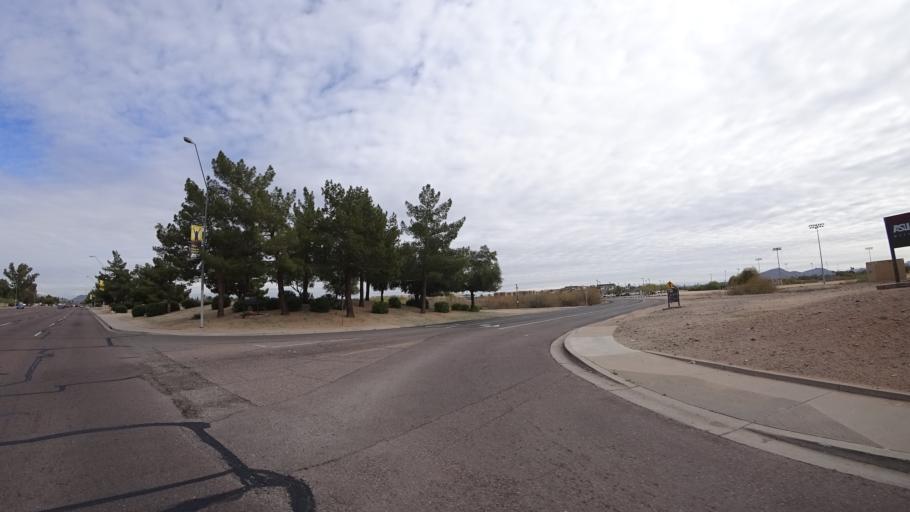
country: US
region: Arizona
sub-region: Maricopa County
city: Glendale
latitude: 33.6053
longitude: -112.1685
